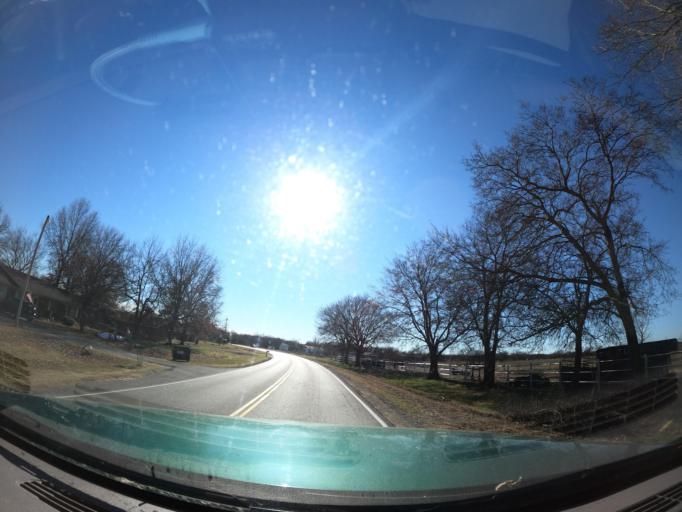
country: US
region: Oklahoma
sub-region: Muskogee County
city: Haskell
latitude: 35.6544
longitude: -95.6555
